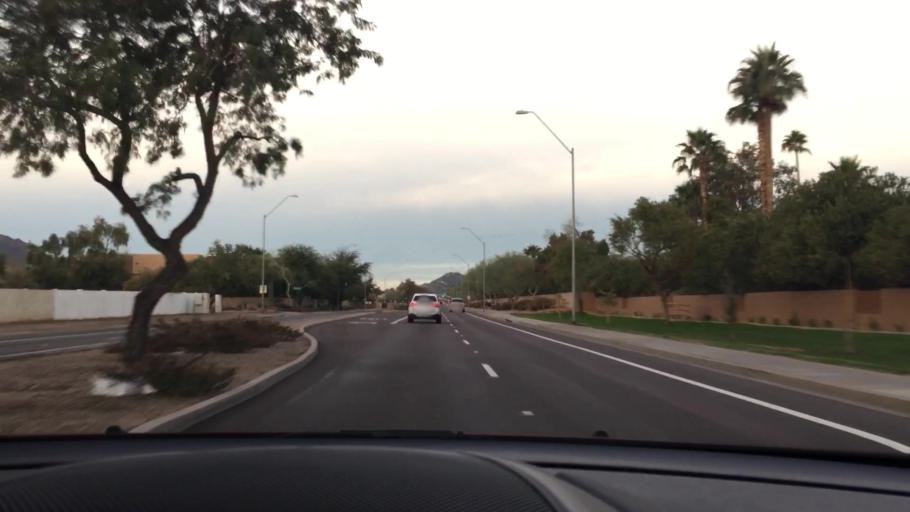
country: US
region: Arizona
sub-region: Maricopa County
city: Scottsdale
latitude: 33.5385
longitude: -111.8991
